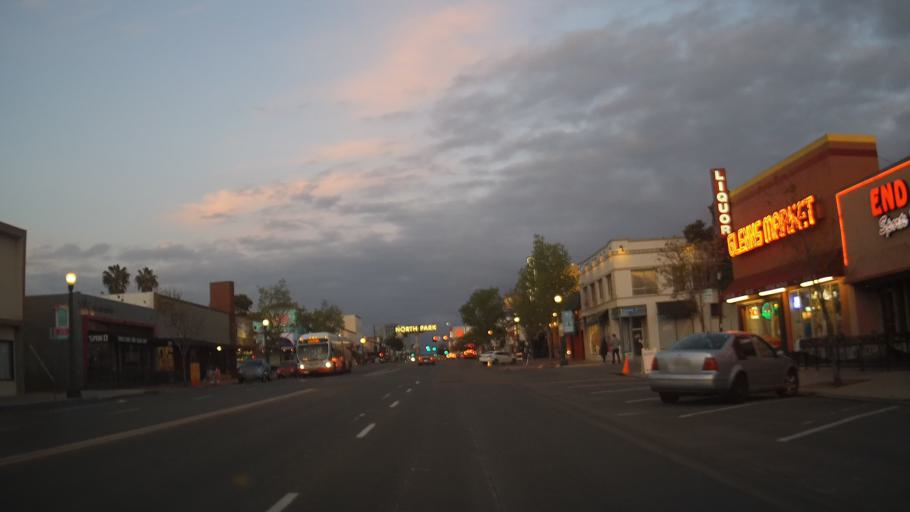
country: US
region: California
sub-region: San Diego County
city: San Diego
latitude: 32.7484
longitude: -117.1324
